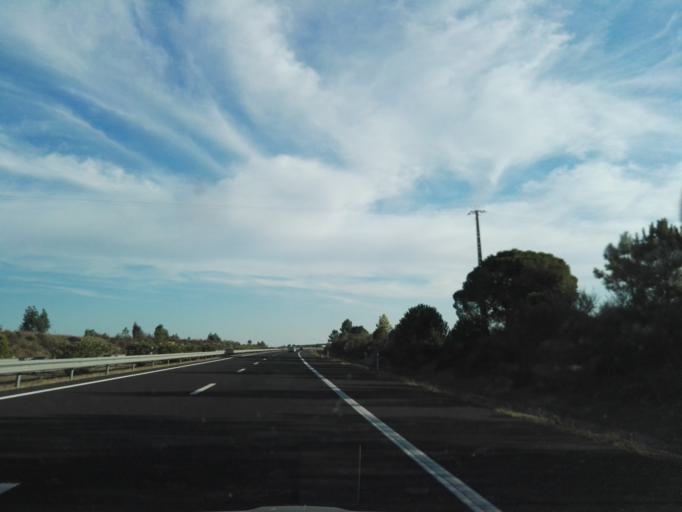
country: PT
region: Santarem
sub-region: Benavente
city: Poceirao
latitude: 38.7842
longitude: -8.6863
